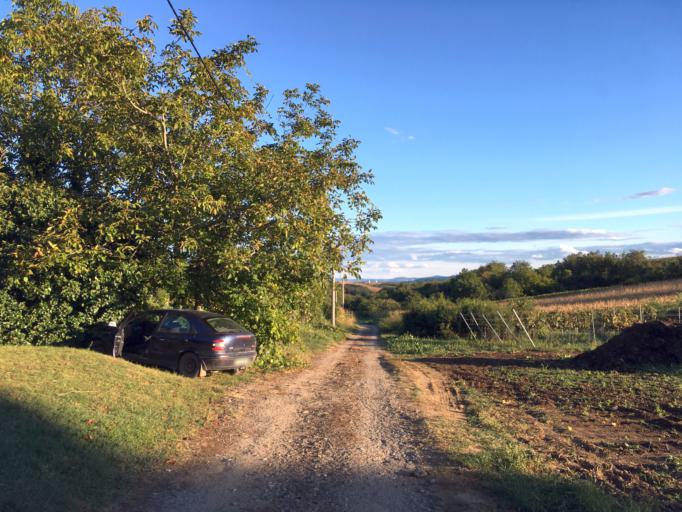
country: SK
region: Nitriansky
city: Svodin
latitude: 47.9152
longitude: 18.4366
